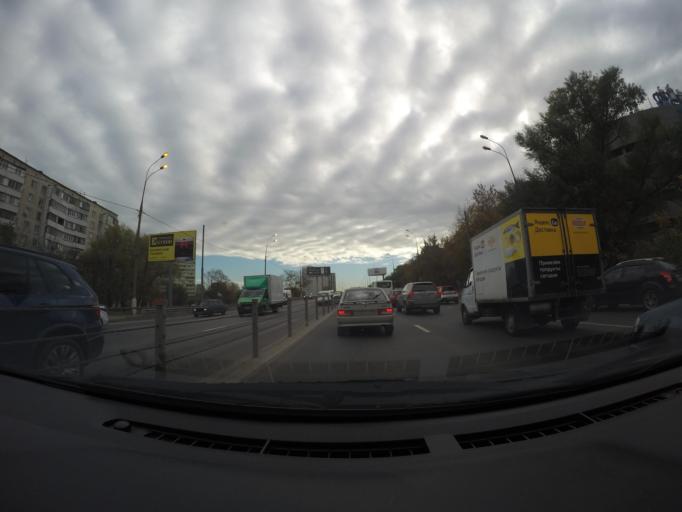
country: RU
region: Moskovskaya
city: Mytishchi
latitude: 55.9211
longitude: 37.7621
